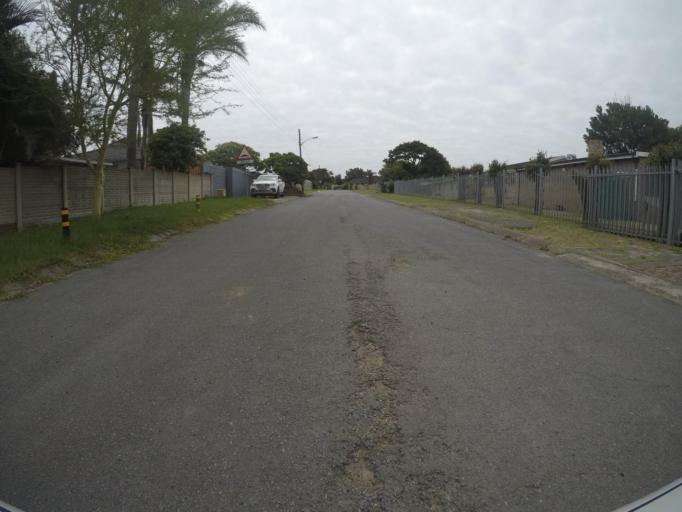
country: ZA
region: Eastern Cape
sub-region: Buffalo City Metropolitan Municipality
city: East London
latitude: -32.9719
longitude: 27.9390
